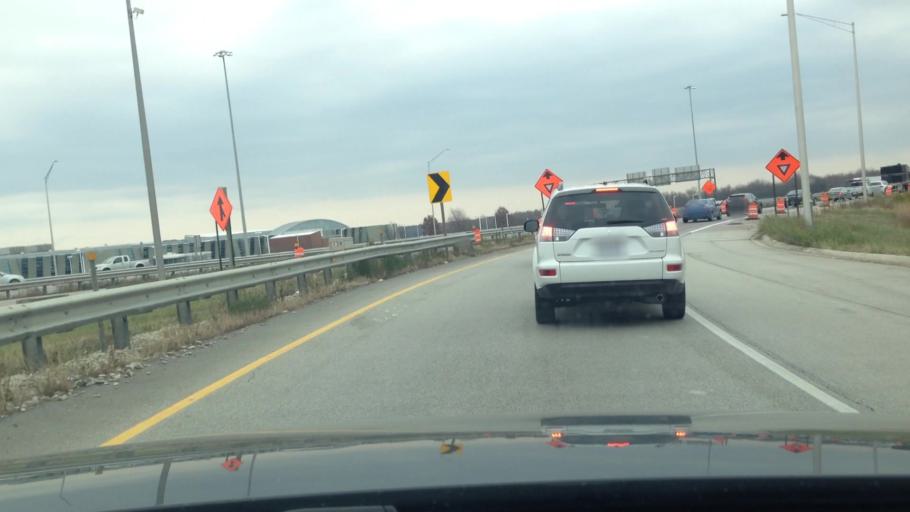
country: US
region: Illinois
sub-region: Cook County
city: Rolling Meadows
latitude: 42.0550
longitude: -88.0294
